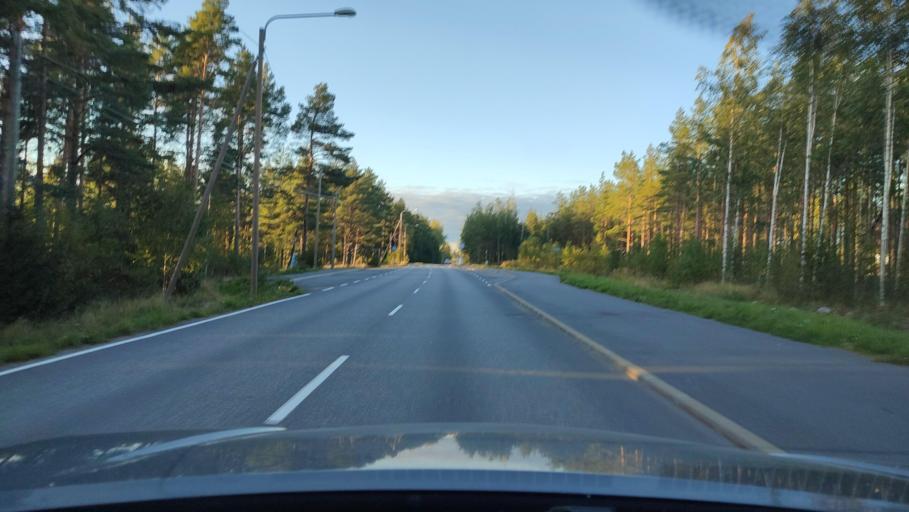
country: FI
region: Ostrobothnia
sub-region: Sydosterbotten
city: Kristinestad
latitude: 62.2348
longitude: 21.5209
